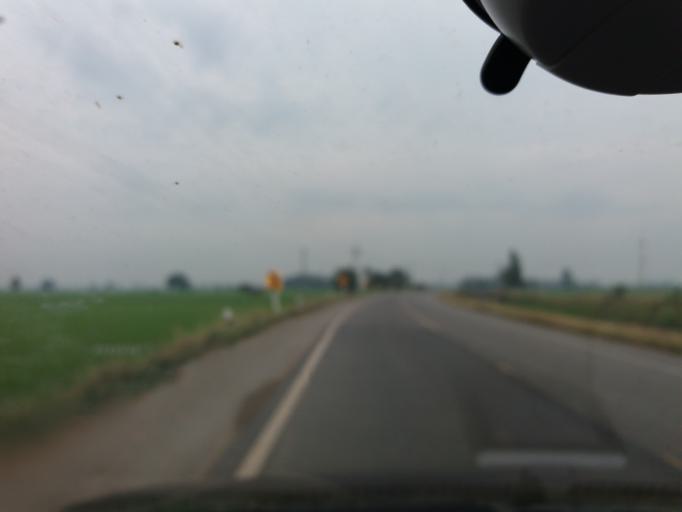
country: TH
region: Suphan Buri
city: Doem Bang Nang Buat
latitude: 14.8752
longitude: 100.1337
